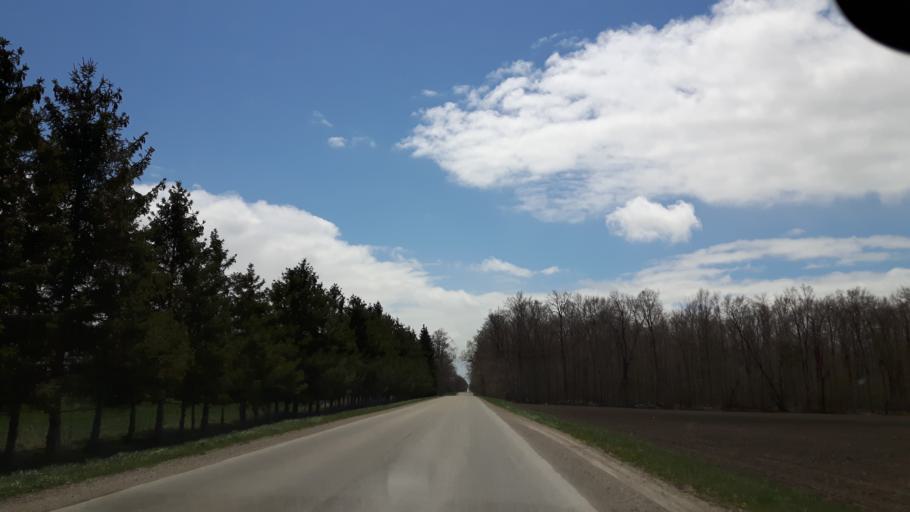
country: CA
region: Ontario
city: Bluewater
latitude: 43.5427
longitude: -81.6751
